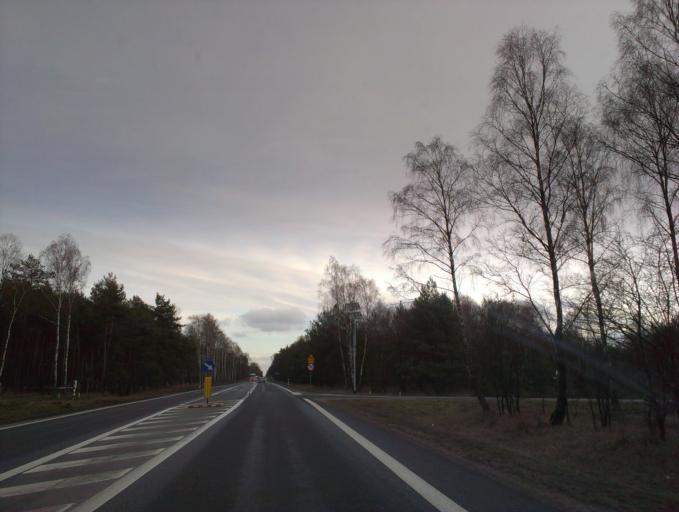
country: PL
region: Masovian Voivodeship
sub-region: Powiat sierpecki
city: Szczutowo
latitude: 52.8855
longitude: 19.5811
